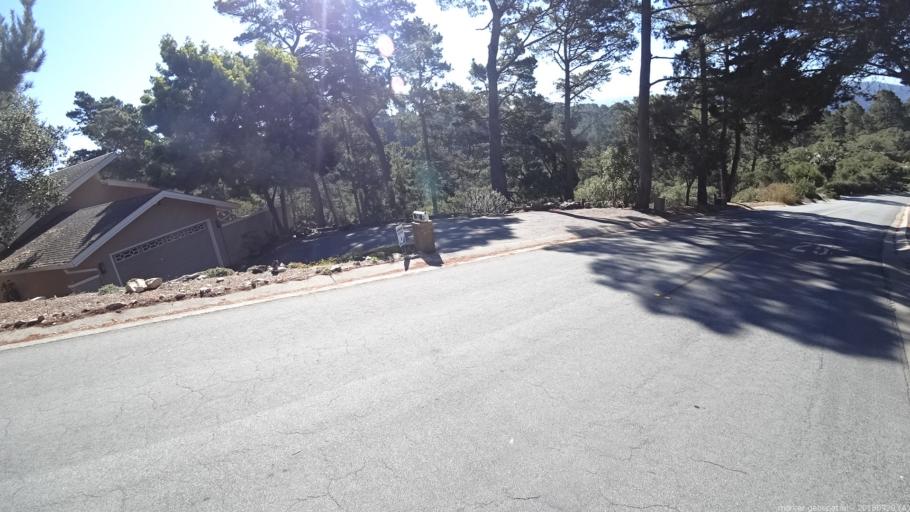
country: US
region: California
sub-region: Monterey County
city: Carmel-by-the-Sea
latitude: 36.5563
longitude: -121.8951
